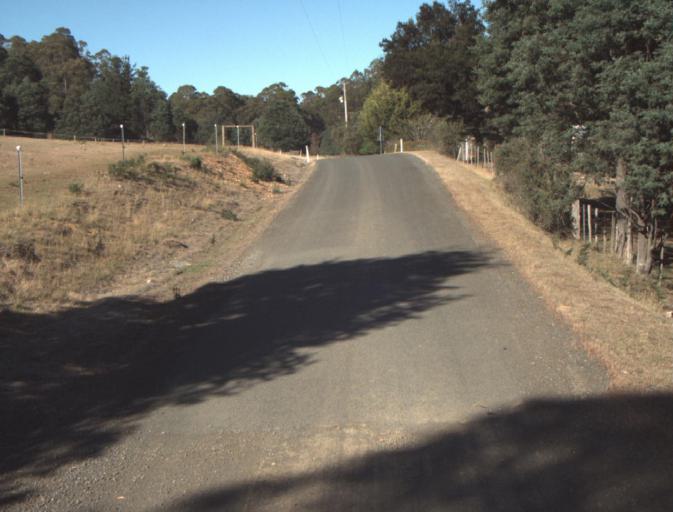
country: AU
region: Tasmania
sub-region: Launceston
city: Newstead
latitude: -41.2966
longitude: 147.3370
